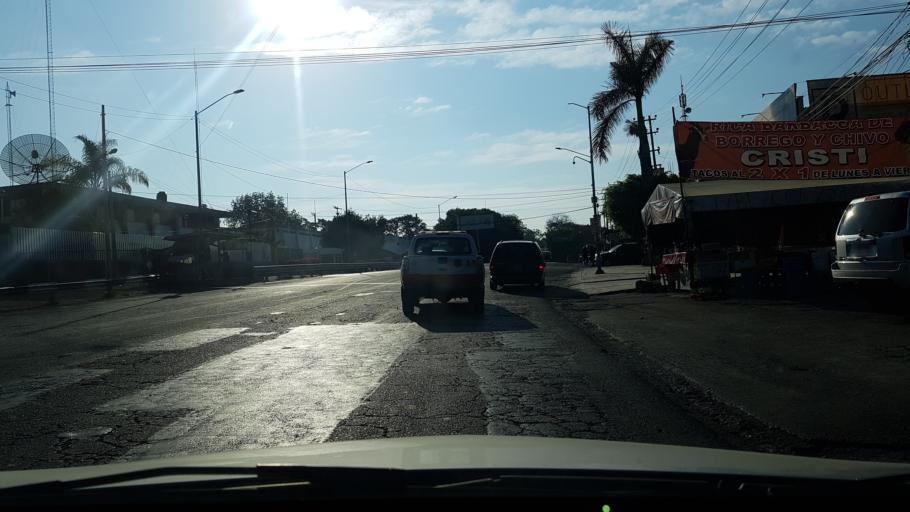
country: MX
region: Morelos
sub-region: Cuernavaca
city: Fraccionamiento Lomas de Ahuatlan
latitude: 18.9678
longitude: -99.2390
